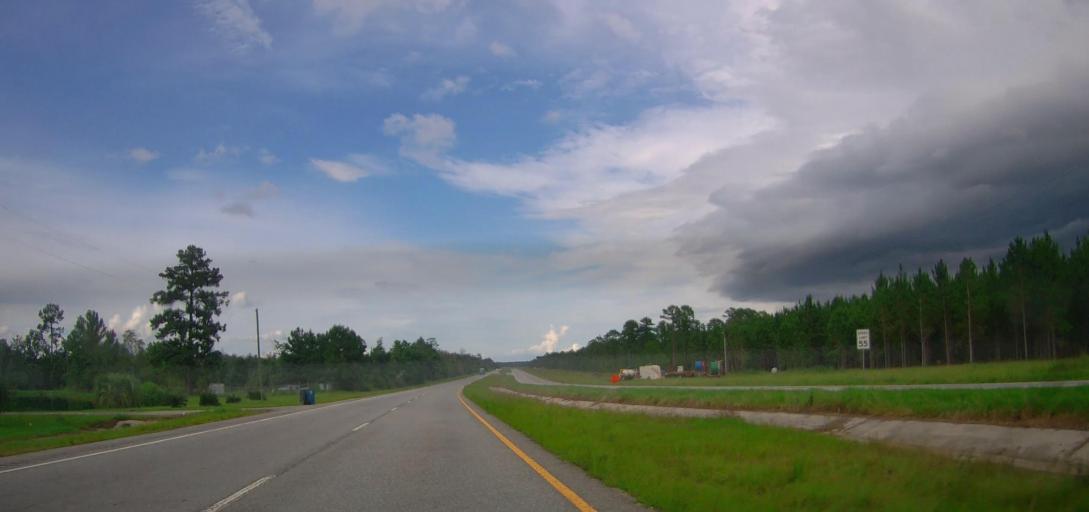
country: US
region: Georgia
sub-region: Pierce County
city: Blackshear
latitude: 31.4335
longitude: -82.0885
